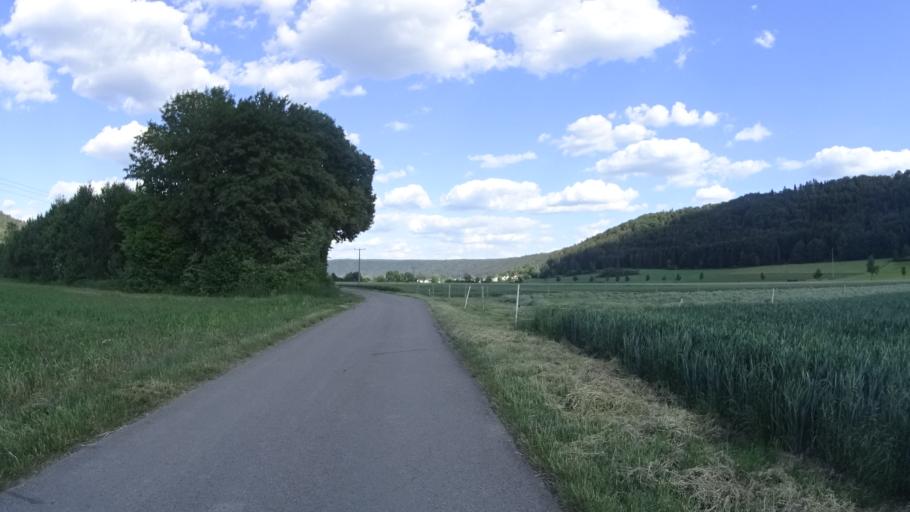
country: DE
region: Bavaria
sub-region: Upper Palatinate
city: Dietfurt
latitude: 49.0211
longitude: 11.5044
